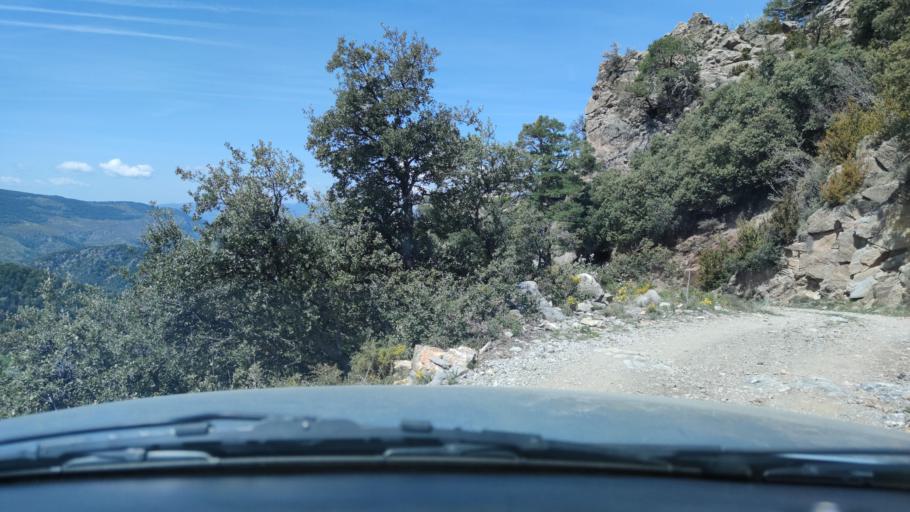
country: ES
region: Catalonia
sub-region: Provincia de Lleida
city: Sort
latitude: 42.3089
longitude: 1.1529
